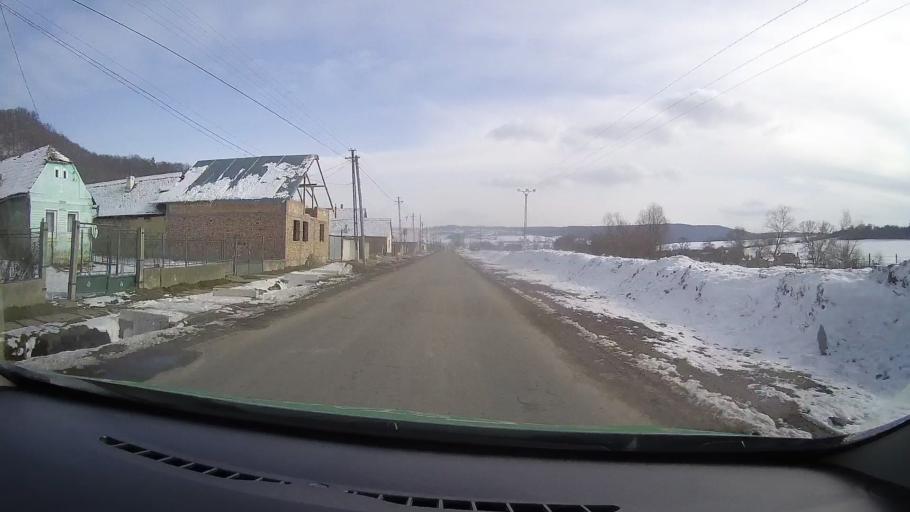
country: RO
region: Sibiu
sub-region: Comuna Iacobeni
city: Iacobeni
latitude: 46.0472
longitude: 24.7229
